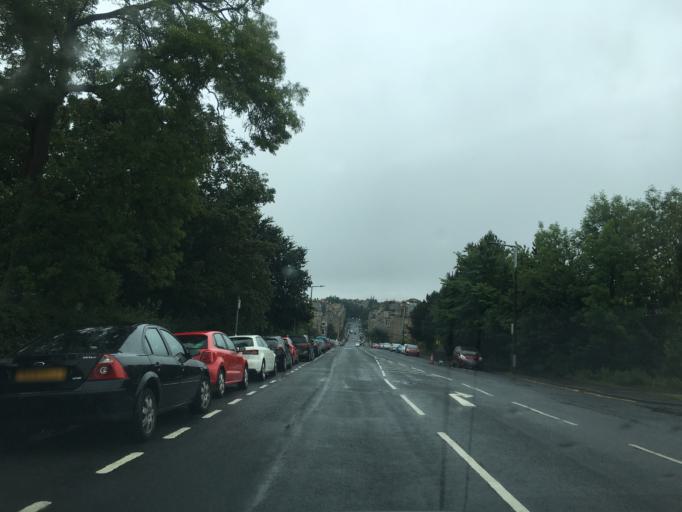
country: GB
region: Scotland
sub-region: Edinburgh
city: Edinburgh
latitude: 55.9615
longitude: -3.2200
